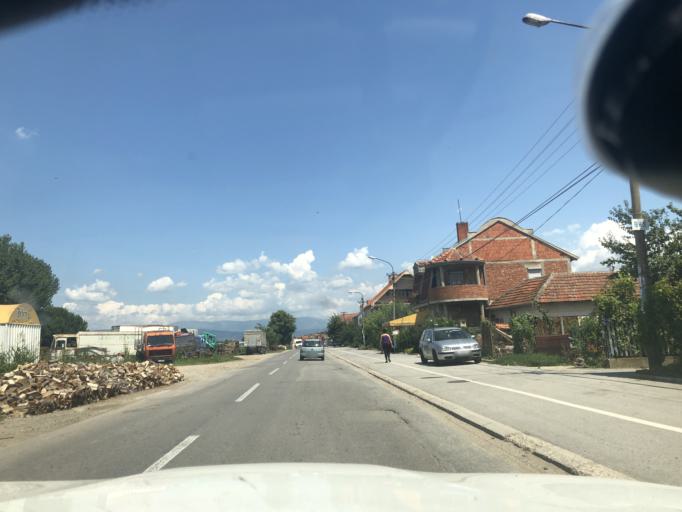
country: RS
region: Central Serbia
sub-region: Jablanicki Okrug
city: Leskovac
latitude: 42.9822
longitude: 21.9131
